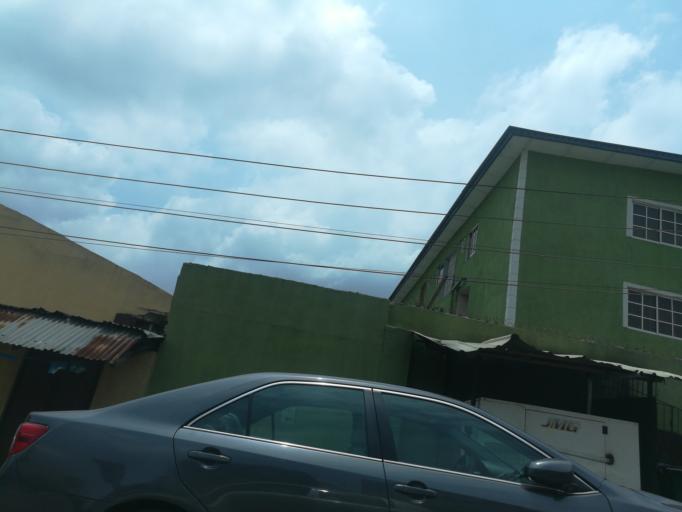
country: NG
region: Lagos
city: Ojota
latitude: 6.5926
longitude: 3.3622
